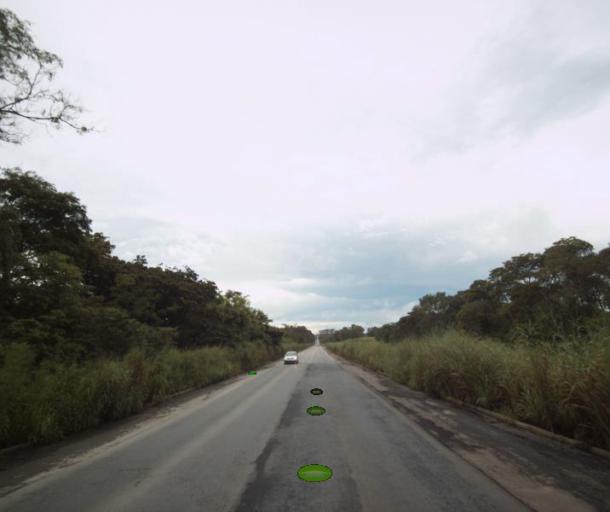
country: BR
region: Goias
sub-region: Porangatu
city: Porangatu
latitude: -13.5522
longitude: -49.0914
